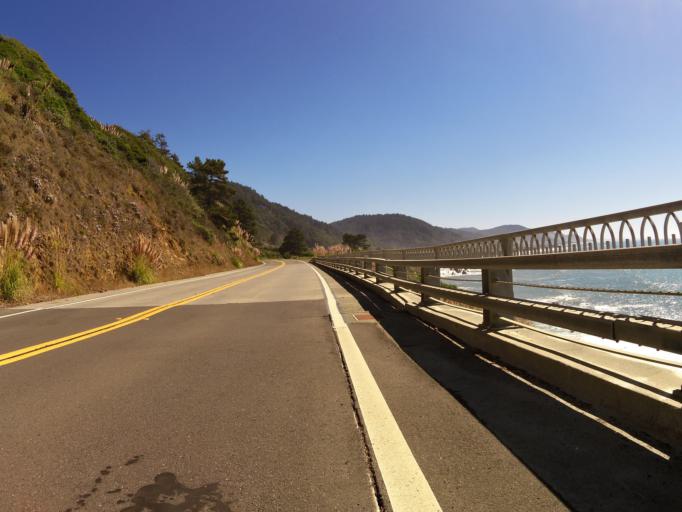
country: US
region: California
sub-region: Mendocino County
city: Fort Bragg
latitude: 39.6939
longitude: -123.7975
